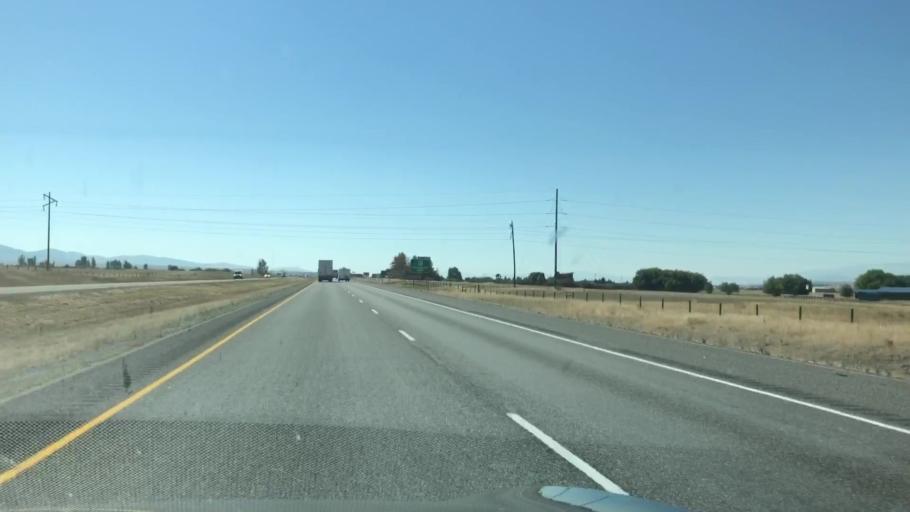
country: US
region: Montana
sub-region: Powell County
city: Deer Lodge
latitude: 46.4311
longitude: -112.7232
